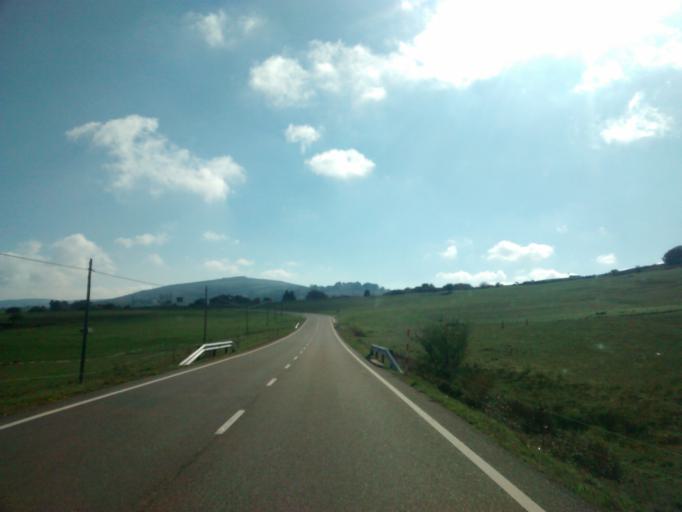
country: ES
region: Cantabria
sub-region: Provincia de Cantabria
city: Reinosa
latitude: 42.9690
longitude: -4.0685
